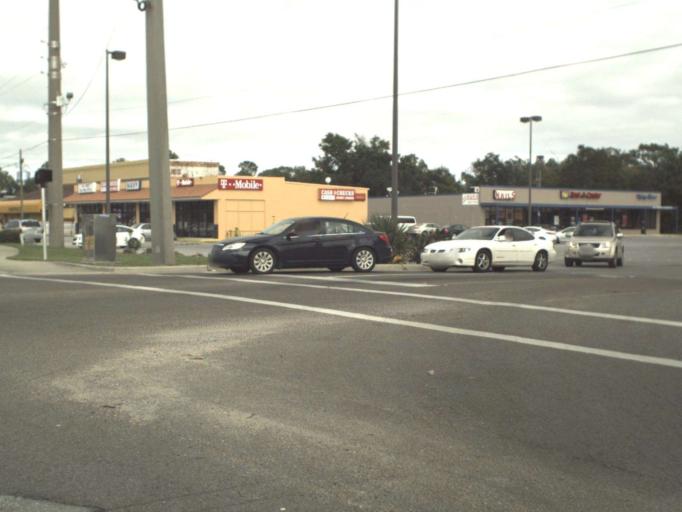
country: US
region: Florida
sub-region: Escambia County
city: Warrington
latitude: 30.3958
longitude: -87.2778
